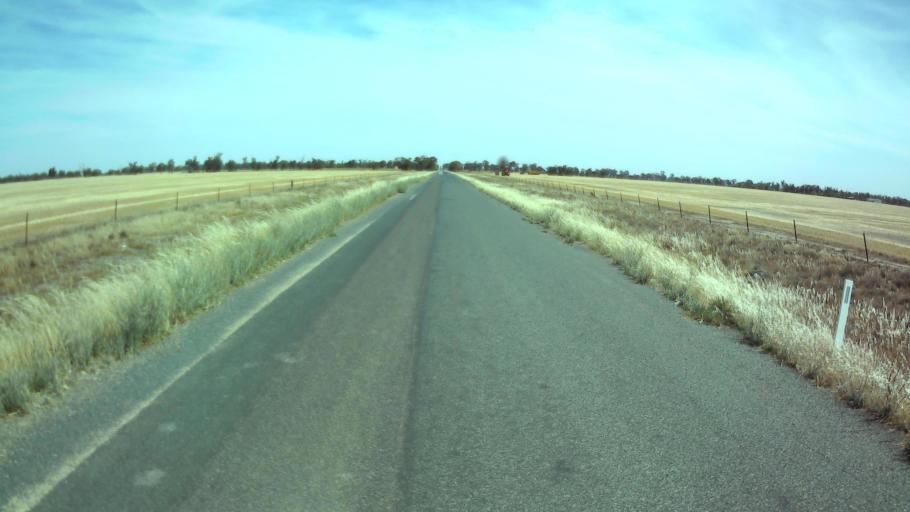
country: AU
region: New South Wales
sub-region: Weddin
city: Grenfell
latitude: -33.9871
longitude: 147.7768
